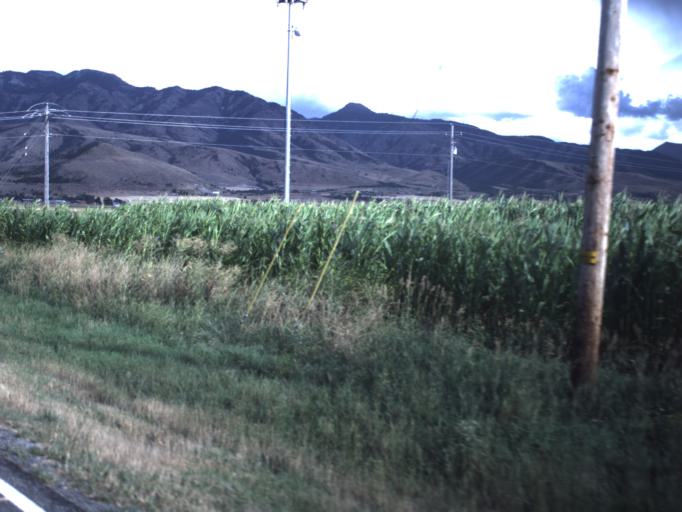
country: US
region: Utah
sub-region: Cache County
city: Lewiston
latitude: 41.9761
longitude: -111.8313
